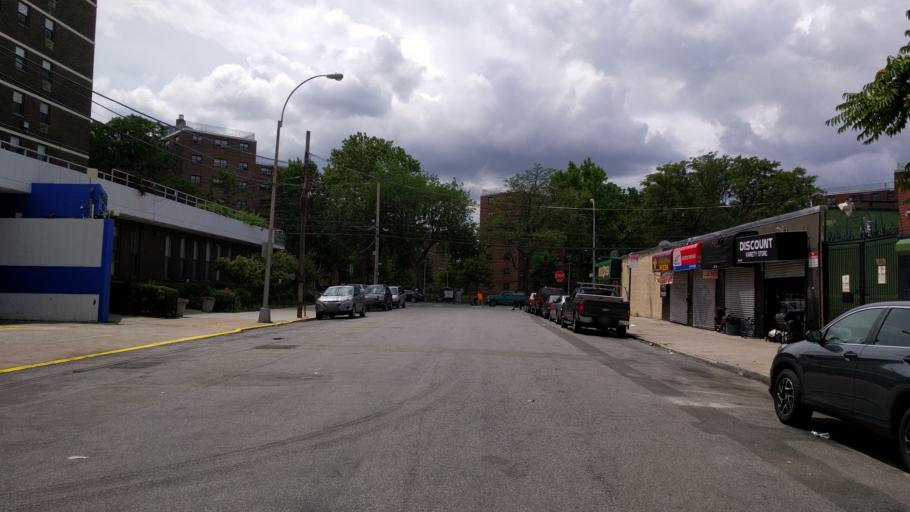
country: US
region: New York
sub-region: New York County
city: Manhattan
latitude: 40.7753
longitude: -73.9331
